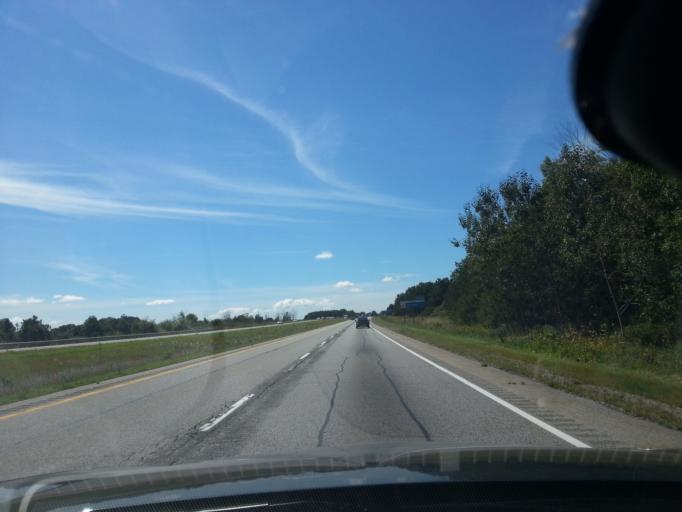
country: CA
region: Ontario
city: Gananoque
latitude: 44.3533
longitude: -76.1000
